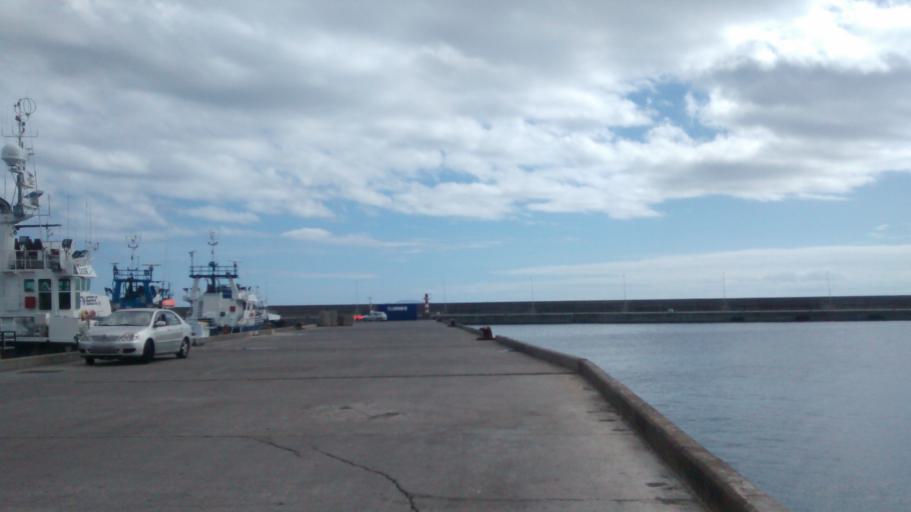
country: PT
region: Madeira
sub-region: Machico
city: Canical
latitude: 32.7358
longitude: -16.7355
